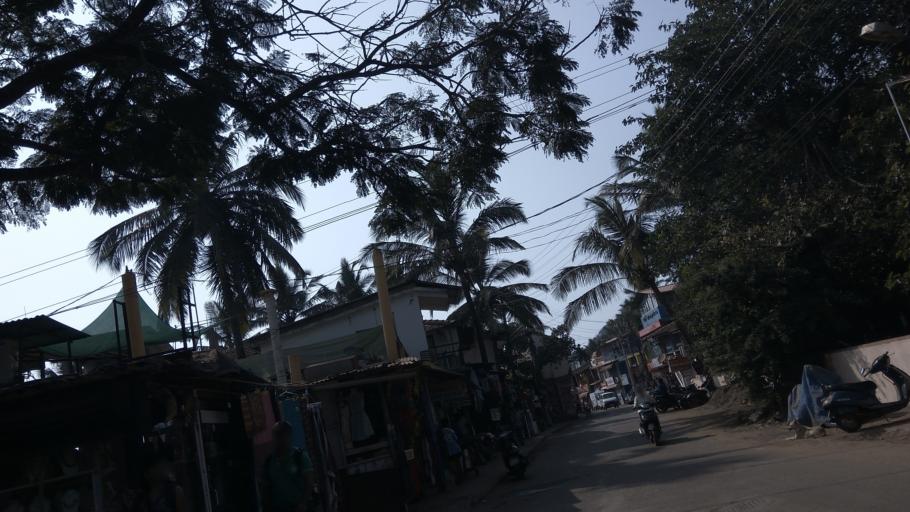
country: IN
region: Goa
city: Calangute
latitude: 15.5615
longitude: 73.7513
